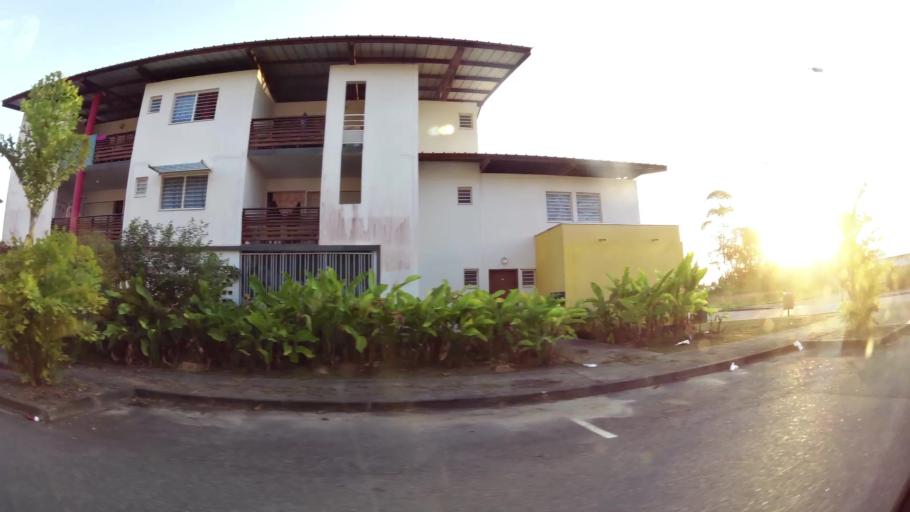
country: GF
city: Macouria
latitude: 4.9310
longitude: -52.4100
